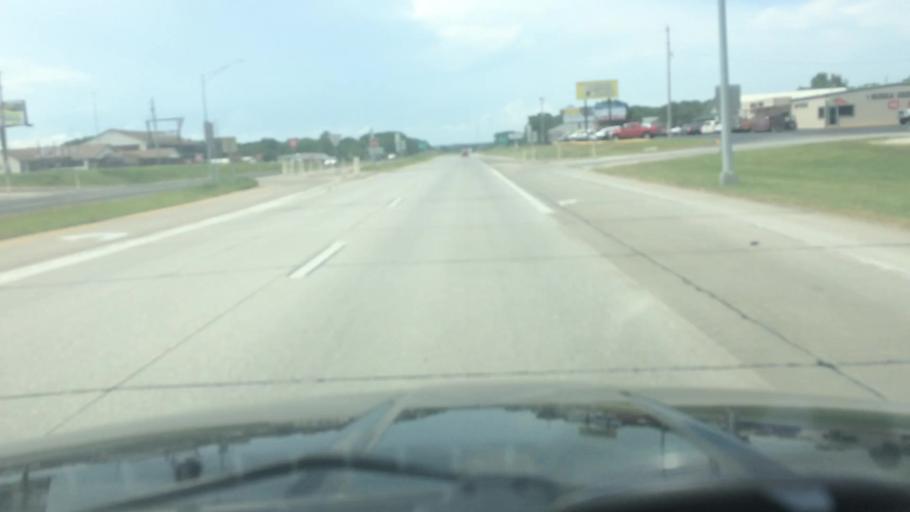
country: US
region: Missouri
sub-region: Saint Clair County
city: Osceola
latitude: 38.0726
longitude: -93.6998
